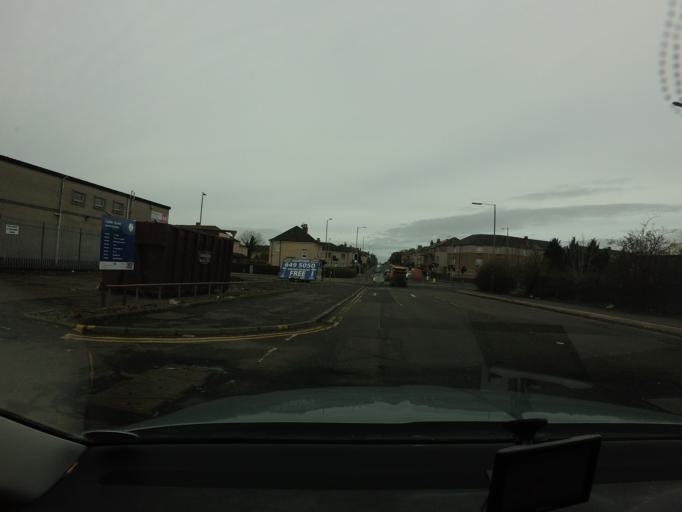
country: GB
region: Scotland
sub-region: Glasgow City
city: Glasgow
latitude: 55.8354
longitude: -4.2480
